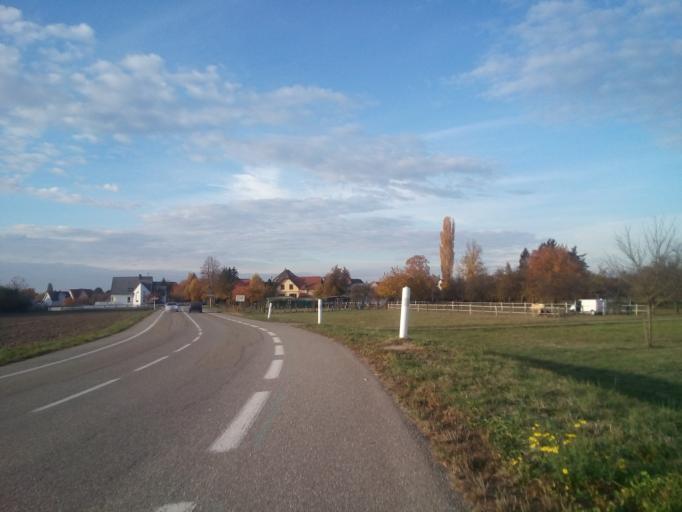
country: FR
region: Alsace
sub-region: Departement du Bas-Rhin
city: Herrlisheim
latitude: 48.7219
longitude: 7.9105
